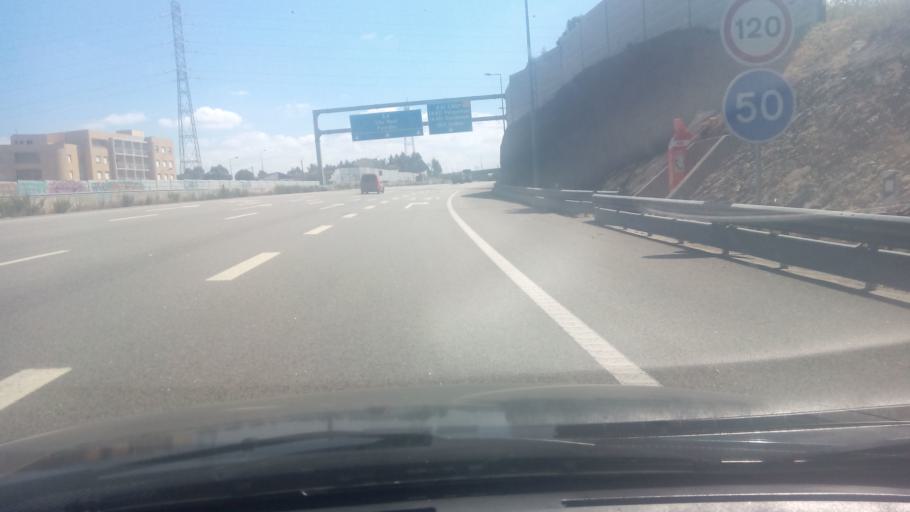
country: PT
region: Porto
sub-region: Valongo
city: Campo
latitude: 41.1826
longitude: -8.4493
